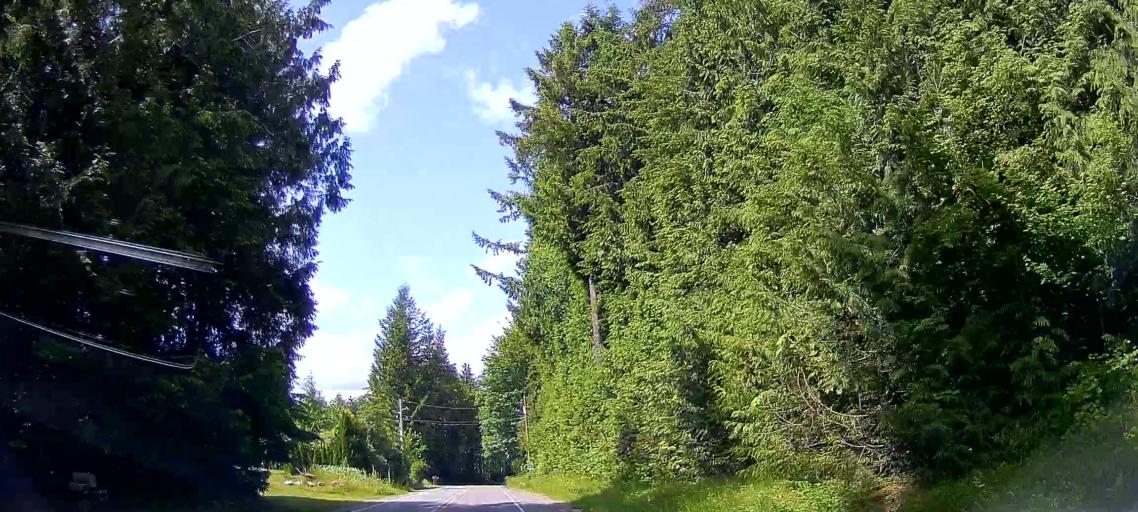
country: US
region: Washington
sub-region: Skagit County
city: Sedro-Woolley
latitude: 48.5560
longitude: -122.2116
